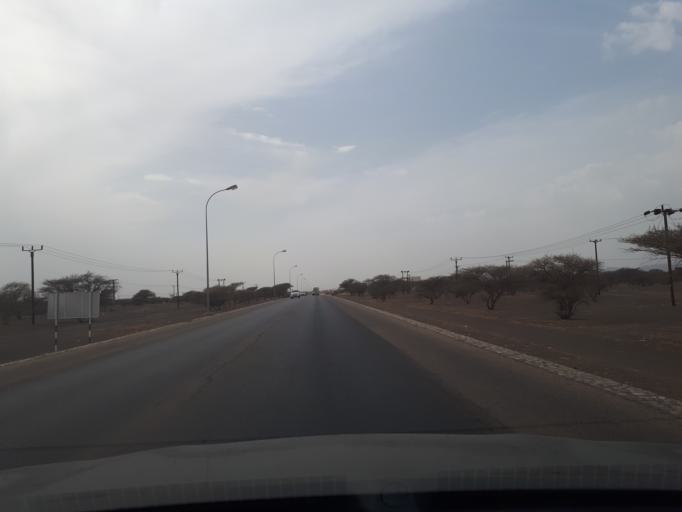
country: OM
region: Ash Sharqiyah
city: Badiyah
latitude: 22.4752
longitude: 58.7848
